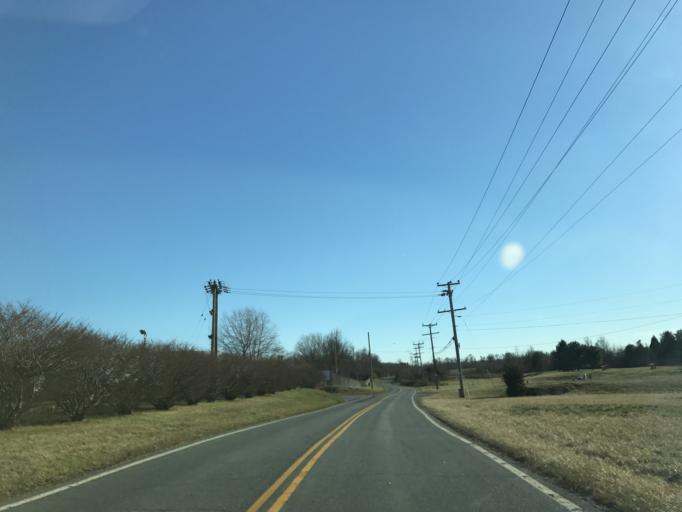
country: US
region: Maryland
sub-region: Harford County
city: Perryman
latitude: 39.4414
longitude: -76.2157
